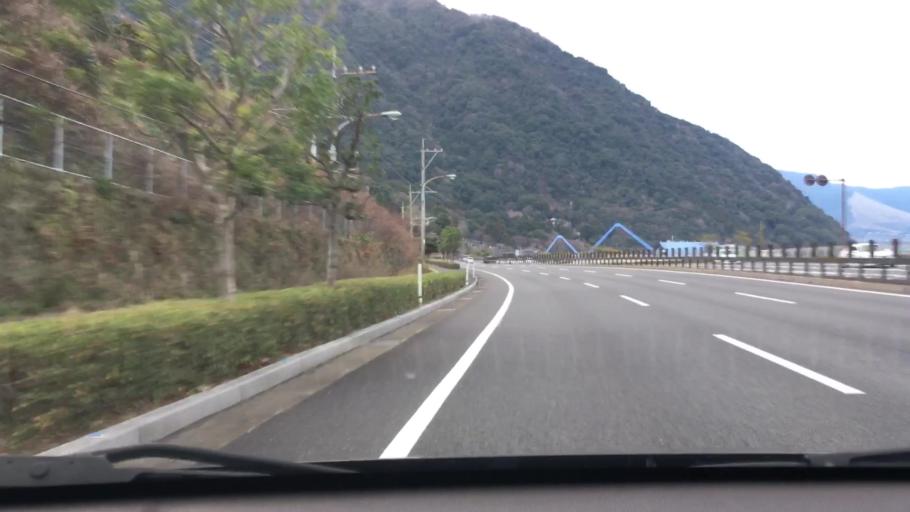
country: JP
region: Oita
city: Beppu
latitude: 33.2569
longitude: 131.5418
